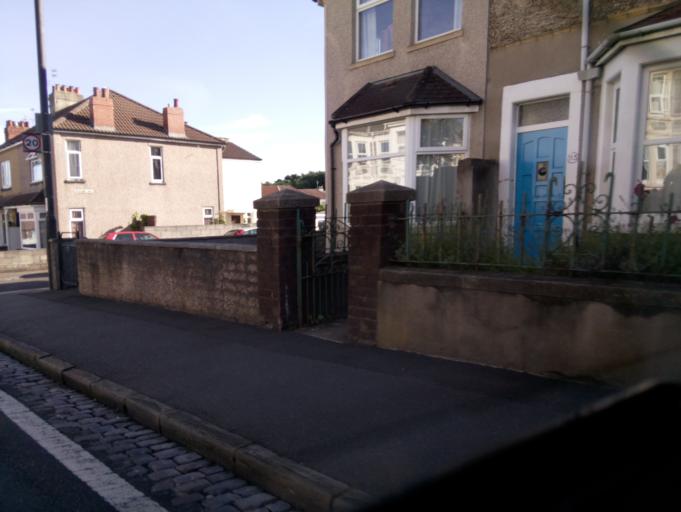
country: GB
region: England
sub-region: South Gloucestershire
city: Kingswood
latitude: 51.4510
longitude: -2.5476
